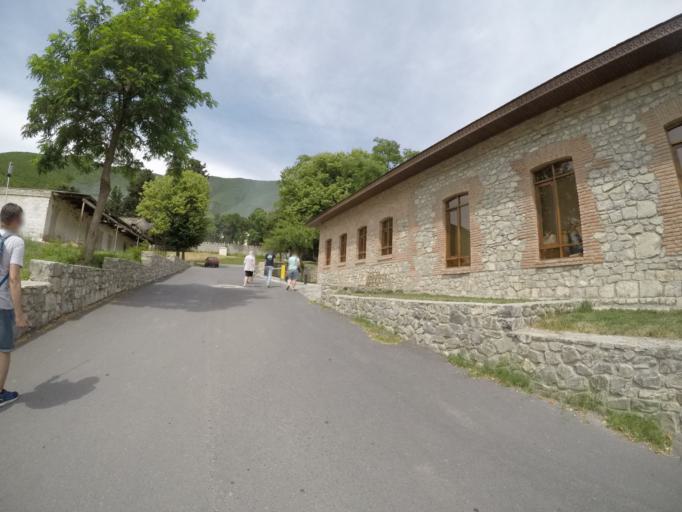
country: AZ
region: Shaki City
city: Sheki
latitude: 41.2043
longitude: 47.1967
